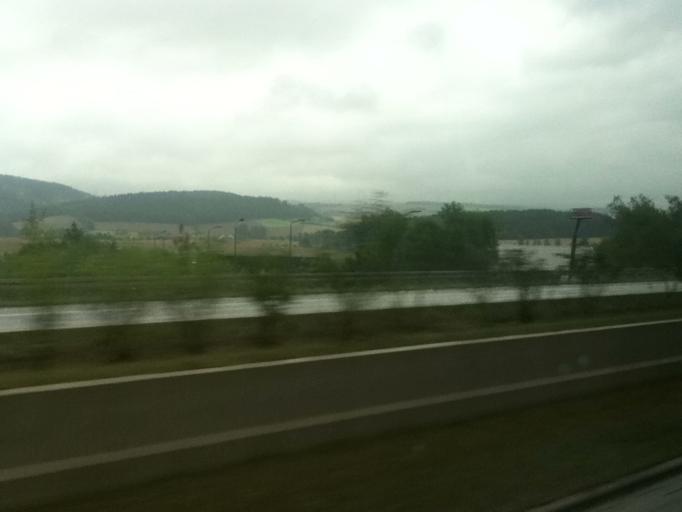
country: DE
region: Thuringia
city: Krauthausen
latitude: 51.0055
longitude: 10.2607
